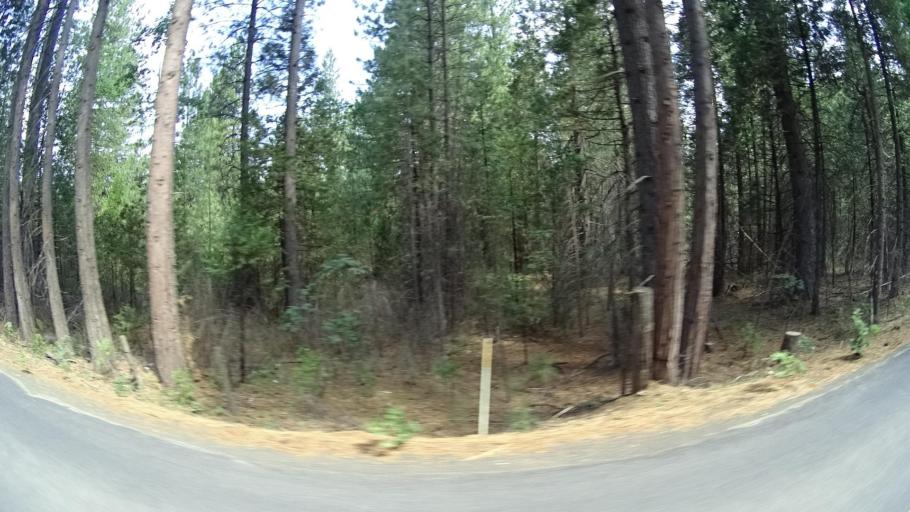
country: US
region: California
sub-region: Tuolumne County
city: Tuolumne City
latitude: 37.7721
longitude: -120.1707
